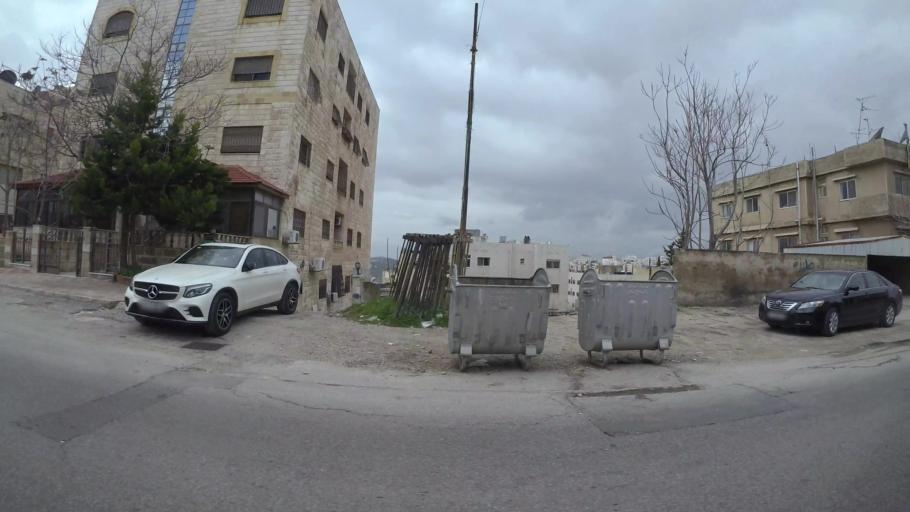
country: JO
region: Amman
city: Wadi as Sir
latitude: 31.9582
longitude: 35.8351
